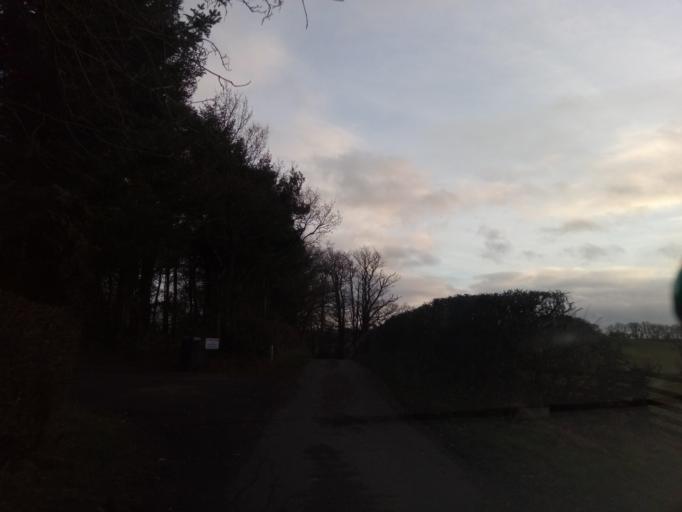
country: GB
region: Scotland
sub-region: The Scottish Borders
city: Newtown St Boswells
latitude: 55.5309
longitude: -2.7048
